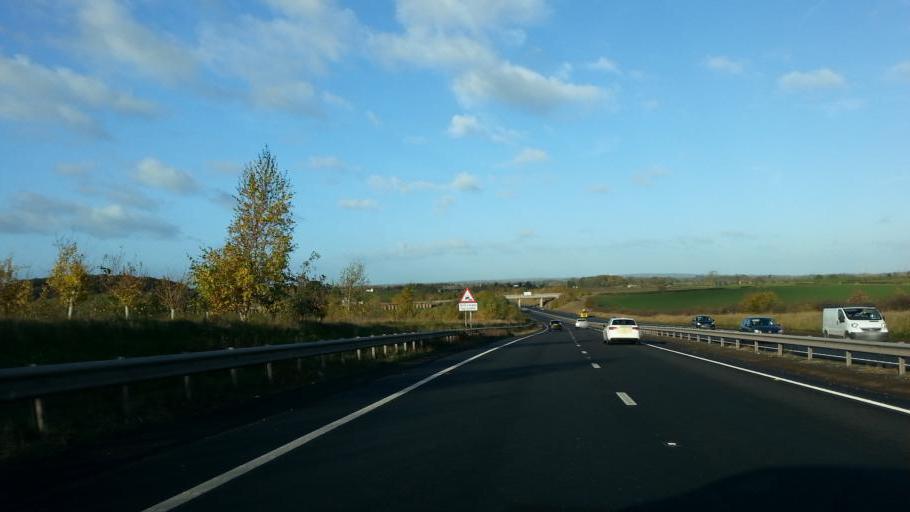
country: GB
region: England
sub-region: Staffordshire
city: Whittington
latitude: 52.6316
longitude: -1.7735
